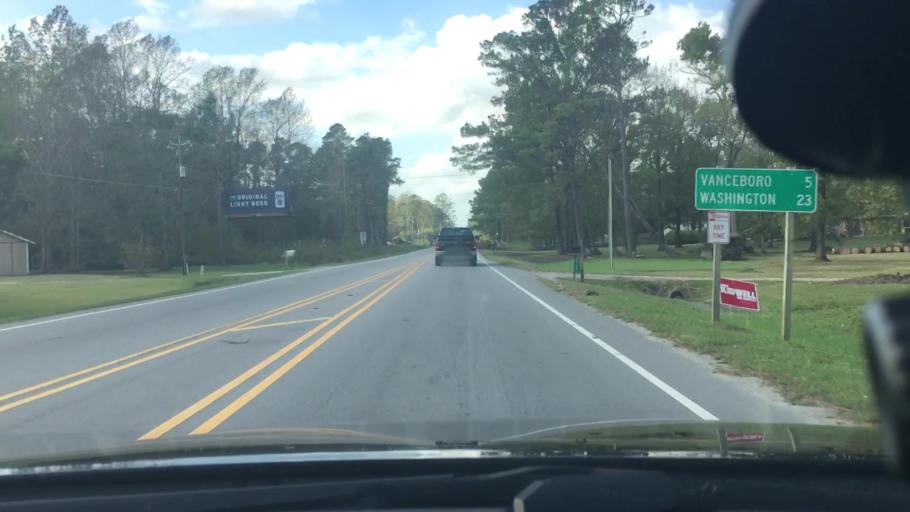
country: US
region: North Carolina
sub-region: Craven County
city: Vanceboro
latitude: 35.2509
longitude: -77.0901
